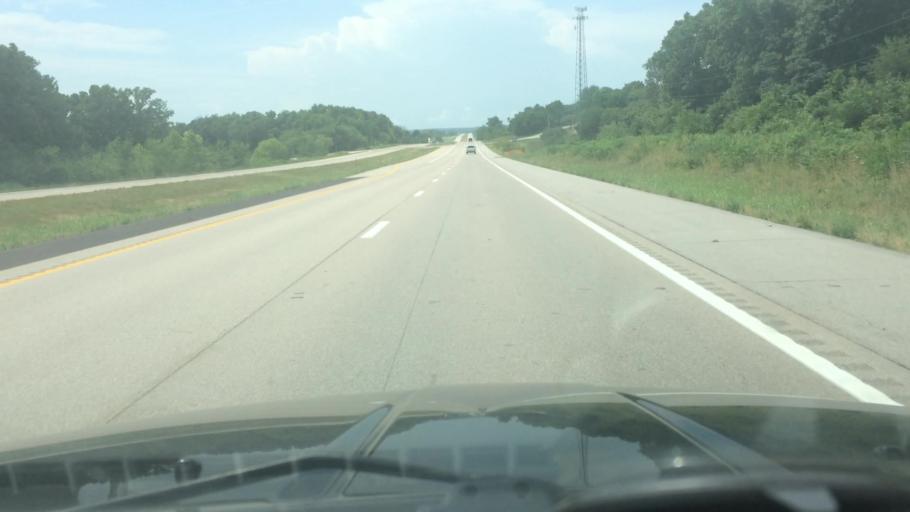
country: US
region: Missouri
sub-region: Polk County
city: Humansville
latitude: 37.7780
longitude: -93.5726
